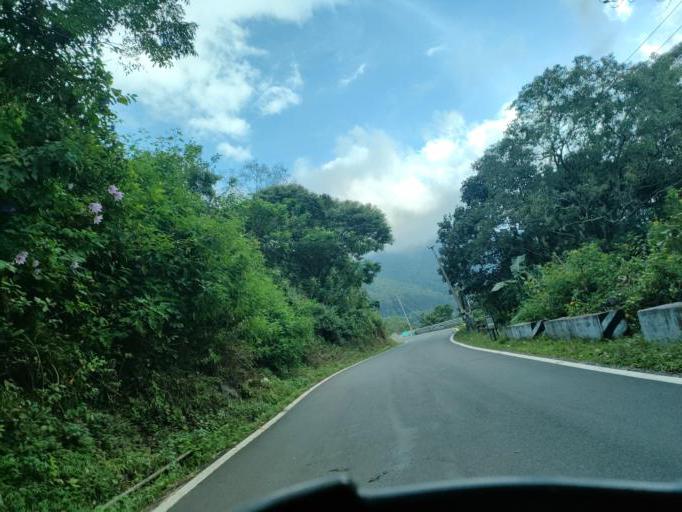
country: IN
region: Tamil Nadu
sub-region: Dindigul
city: Kodaikanal
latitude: 10.2681
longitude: 77.5341
